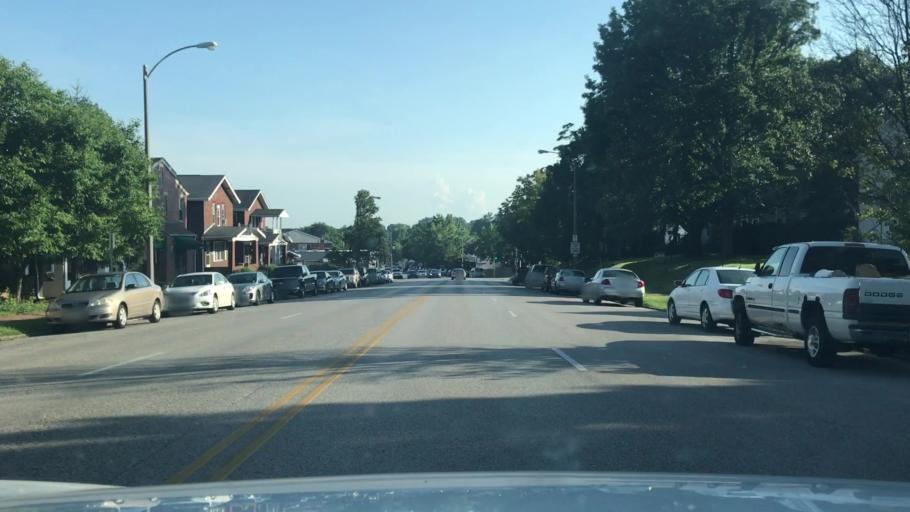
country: US
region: Missouri
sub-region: Saint Louis County
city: Maplewood
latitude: 38.6037
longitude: -90.2982
